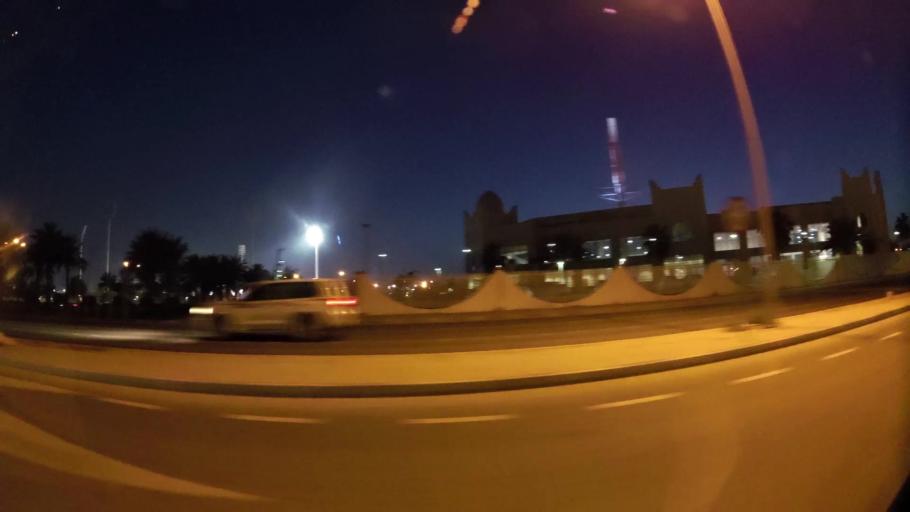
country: QA
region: Baladiyat ar Rayyan
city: Ar Rayyan
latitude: 25.2841
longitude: 51.4314
